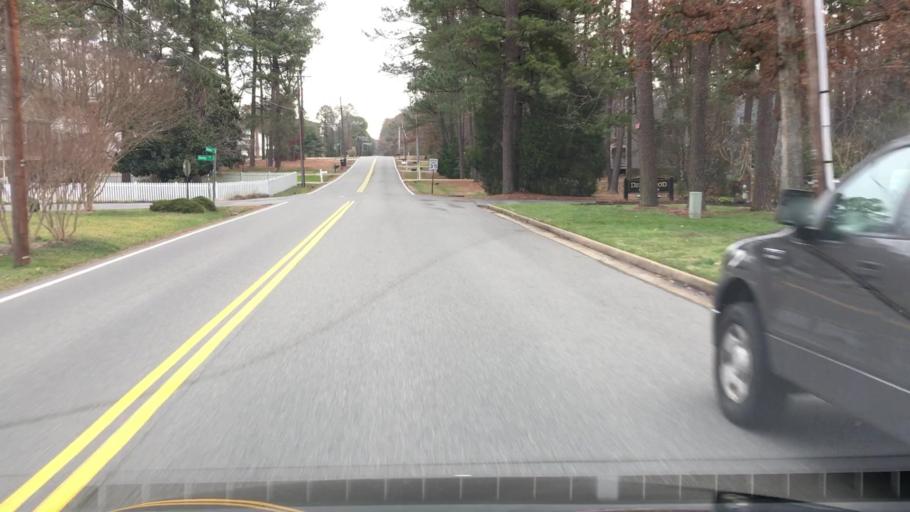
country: US
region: Virginia
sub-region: Henrico County
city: Tuckahoe
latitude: 37.5883
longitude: -77.5830
